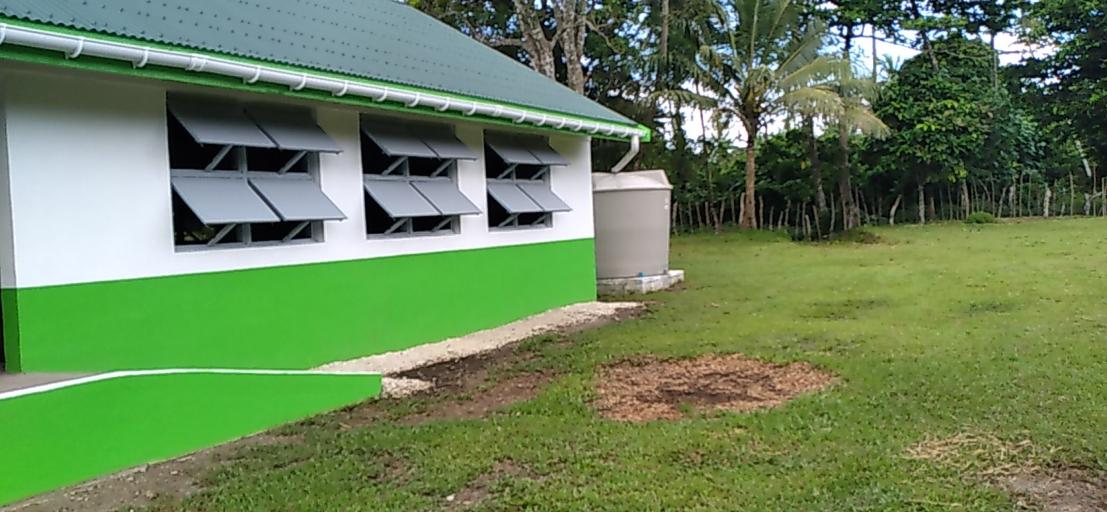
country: VU
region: Shefa
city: Port-Vila
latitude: -16.8812
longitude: 168.5529
